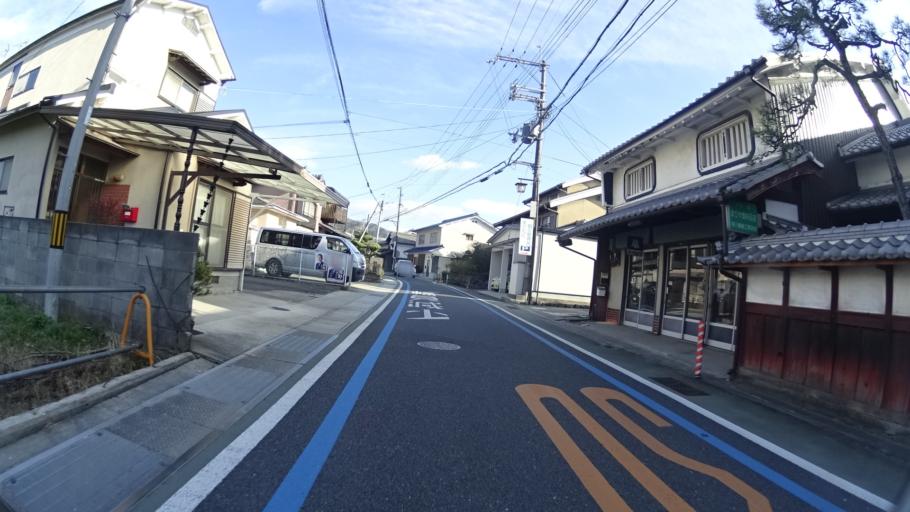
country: JP
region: Kyoto
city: Kameoka
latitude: 35.0044
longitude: 135.6037
